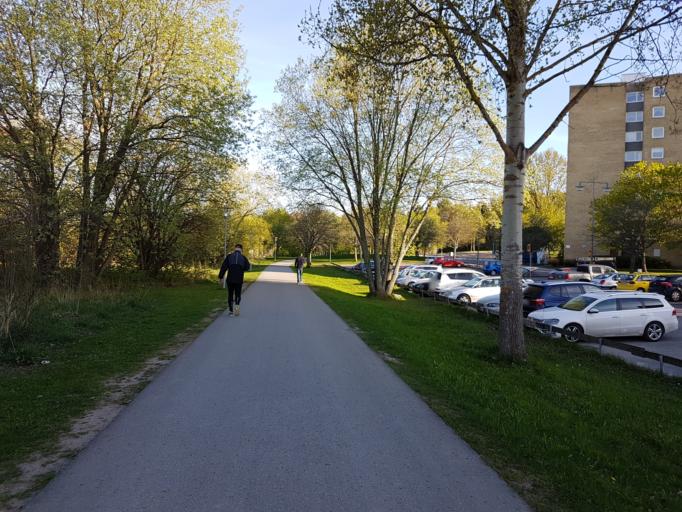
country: SE
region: Stockholm
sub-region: Solna Kommun
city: Rasunda
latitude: 59.3747
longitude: 17.9806
